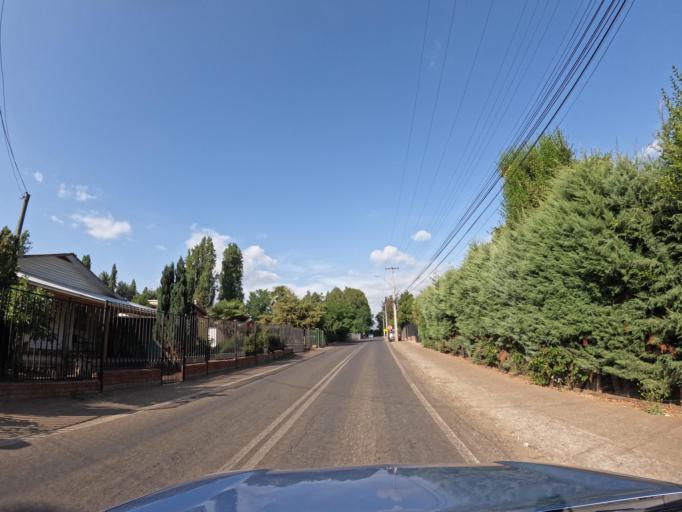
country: CL
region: Maule
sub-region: Provincia de Curico
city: Molina
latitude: -35.2742
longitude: -71.2523
